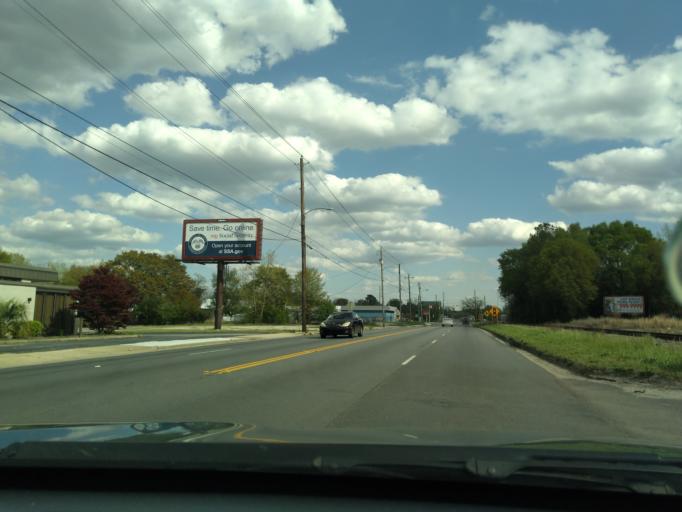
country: US
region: South Carolina
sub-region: Florence County
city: Florence
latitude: 34.2082
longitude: -79.7730
